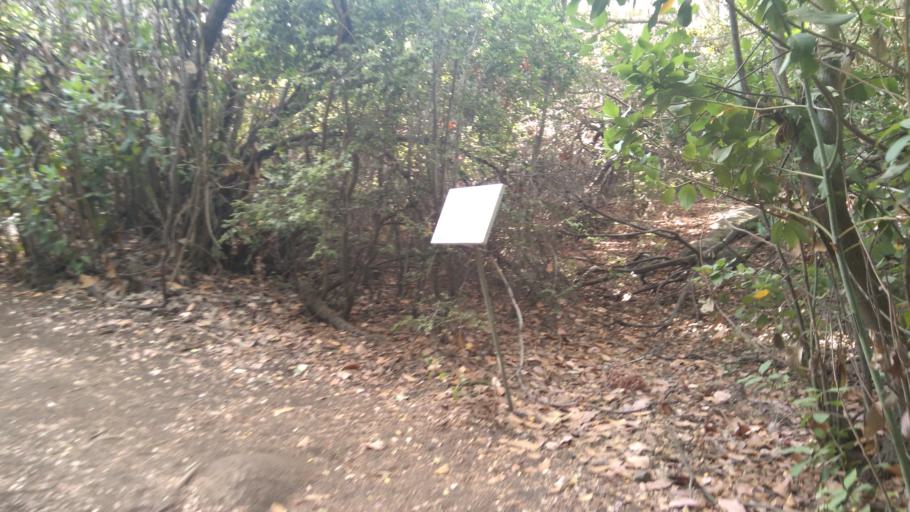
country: CL
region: Santiago Metropolitan
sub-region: Provincia de Cordillera
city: Puente Alto
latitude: -33.7257
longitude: -70.4823
